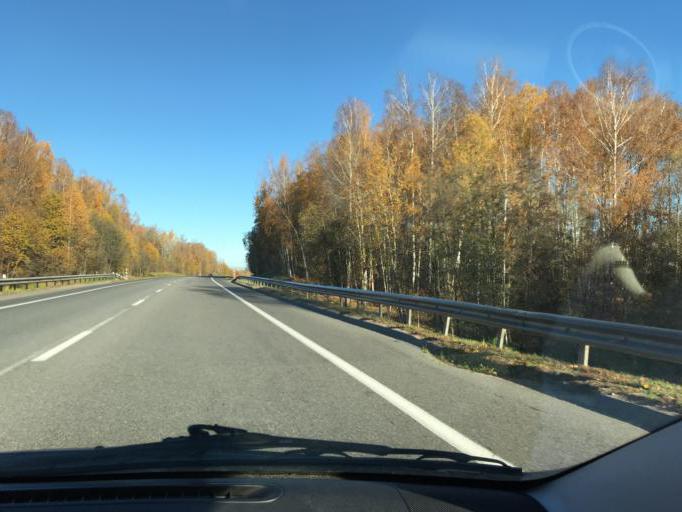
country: BY
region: Vitebsk
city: Vitebsk
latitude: 55.0412
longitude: 30.3169
